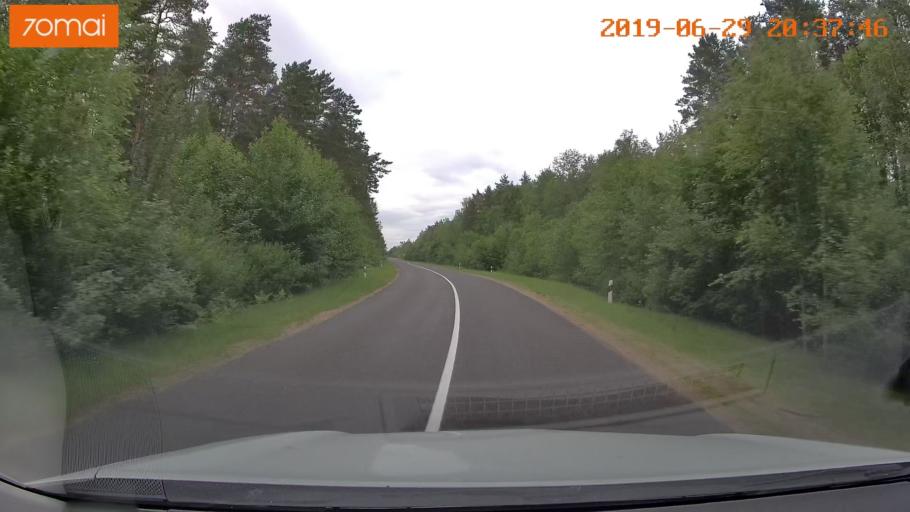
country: BY
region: Brest
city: Hantsavichy
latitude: 52.5423
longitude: 26.3657
